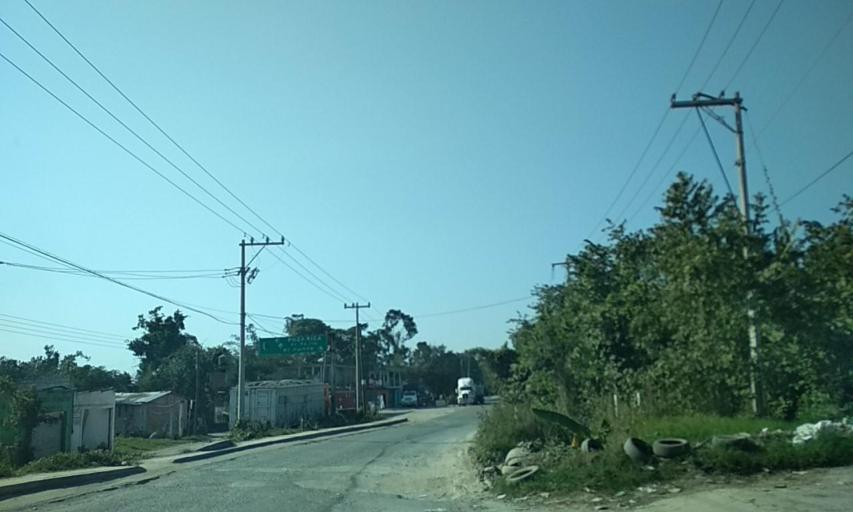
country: MX
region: Veracruz
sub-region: Papantla
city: El Chote
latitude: 20.4029
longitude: -97.3409
